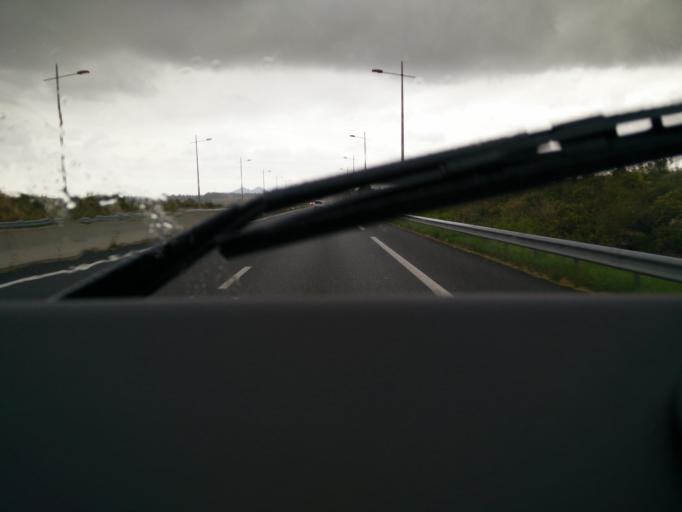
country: FR
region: Nord-Pas-de-Calais
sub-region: Departement du Pas-de-Calais
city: Sains-en-Gohelle
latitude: 50.4353
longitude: 2.6811
